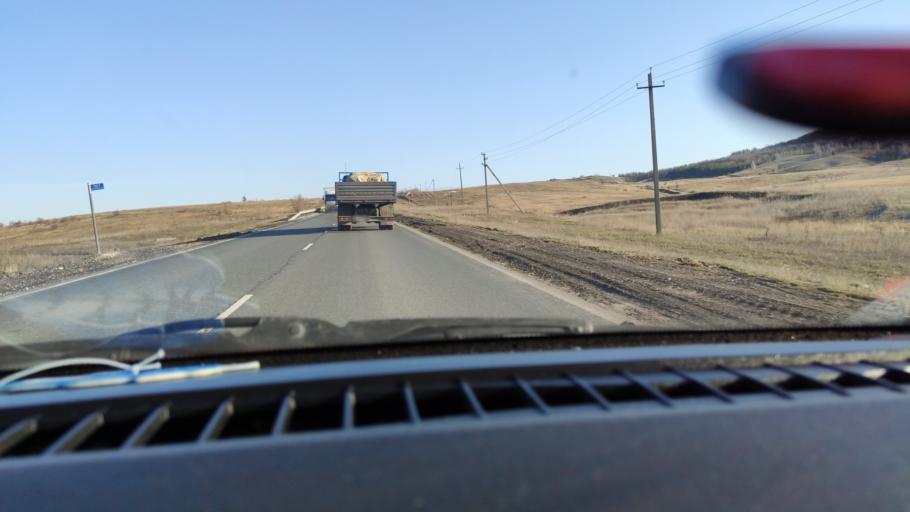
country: RU
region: Saratov
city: Alekseyevka
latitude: 52.3144
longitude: 47.9235
